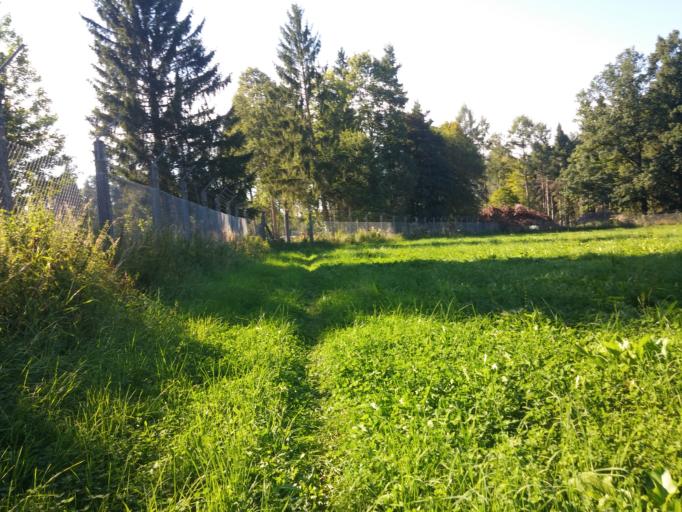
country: DE
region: Baden-Wuerttemberg
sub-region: Tuebingen Region
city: Leutkirch im Allgau
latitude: 47.7880
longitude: 10.0715
